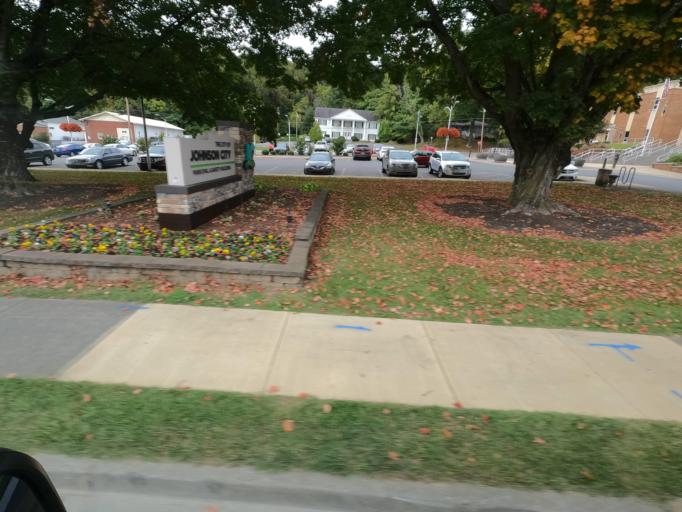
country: US
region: Tennessee
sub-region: Washington County
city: Johnson City
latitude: 36.3206
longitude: -82.3429
